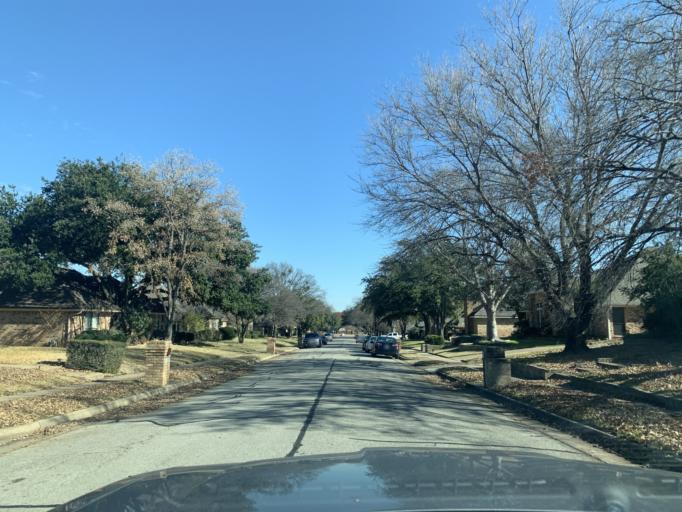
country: US
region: Texas
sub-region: Tarrant County
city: Bedford
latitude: 32.8446
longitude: -97.1569
